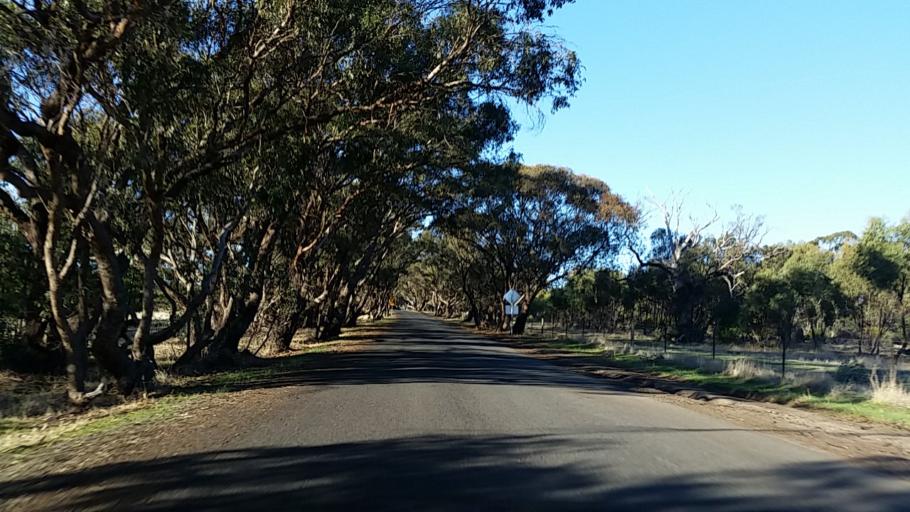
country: AU
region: South Australia
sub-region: Onkaparinga
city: Hackham
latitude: -35.1537
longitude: 138.5532
